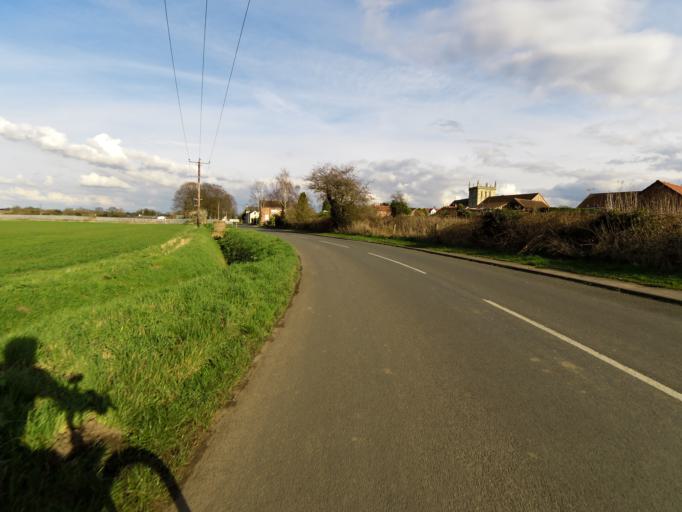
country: GB
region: England
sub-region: East Riding of Yorkshire
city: Snaith
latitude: 53.6926
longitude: -1.0336
